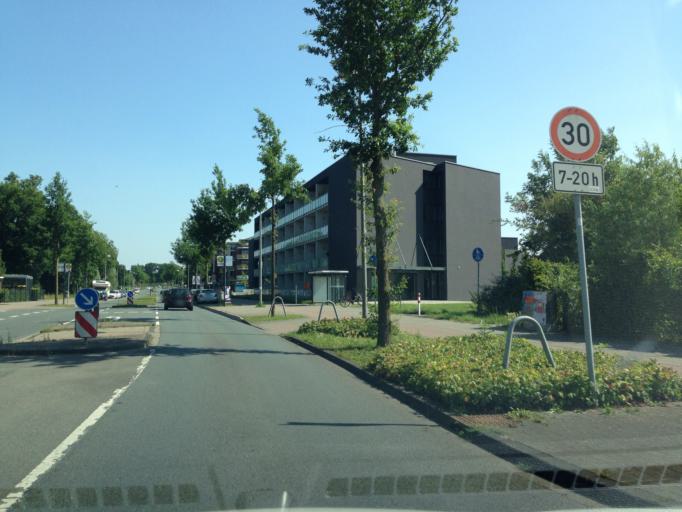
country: DE
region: North Rhine-Westphalia
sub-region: Regierungsbezirk Munster
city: Muenster
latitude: 51.9682
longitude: 7.5623
